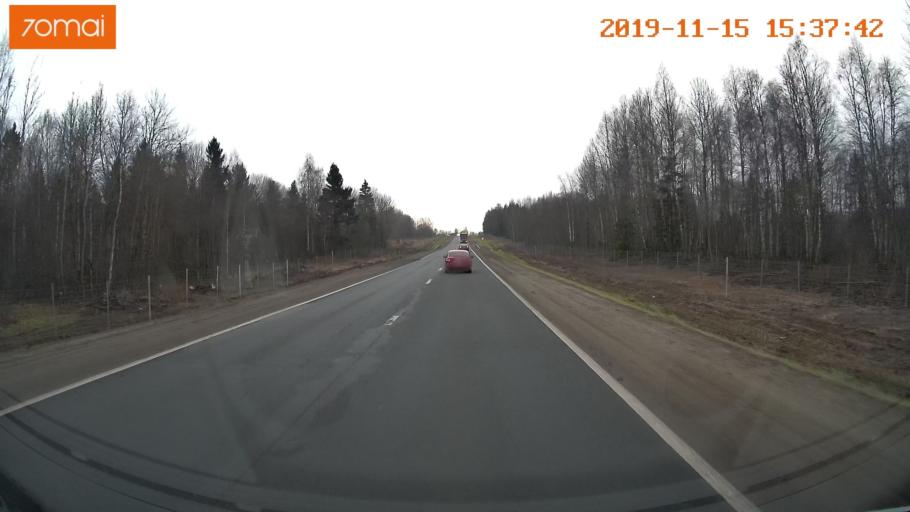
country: RU
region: Jaroslavl
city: Danilov
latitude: 58.0369
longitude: 40.0871
